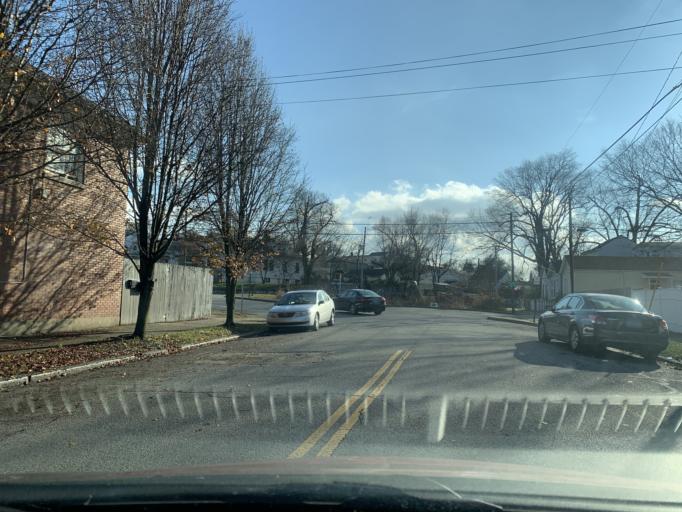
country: US
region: Kentucky
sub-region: Jefferson County
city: Louisville
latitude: 38.2328
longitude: -85.7373
